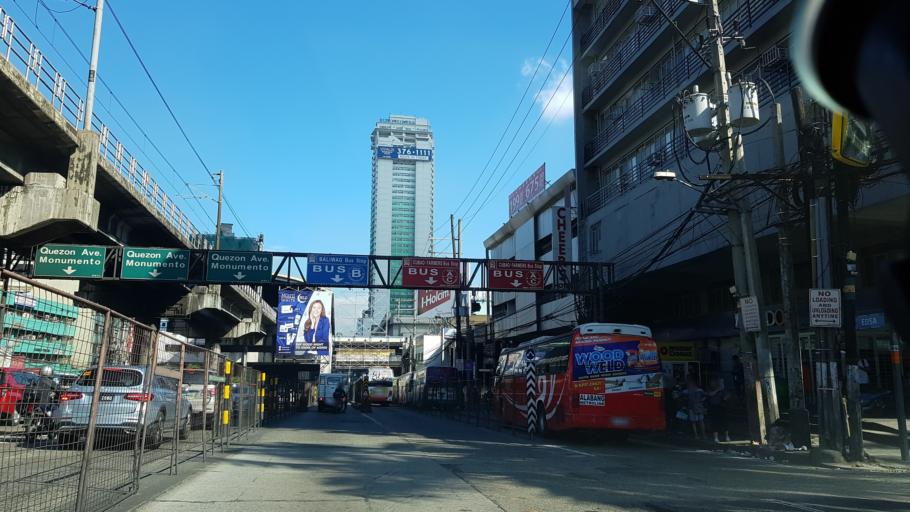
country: PH
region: Metro Manila
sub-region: San Juan
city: San Juan
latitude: 14.6180
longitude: 121.0519
